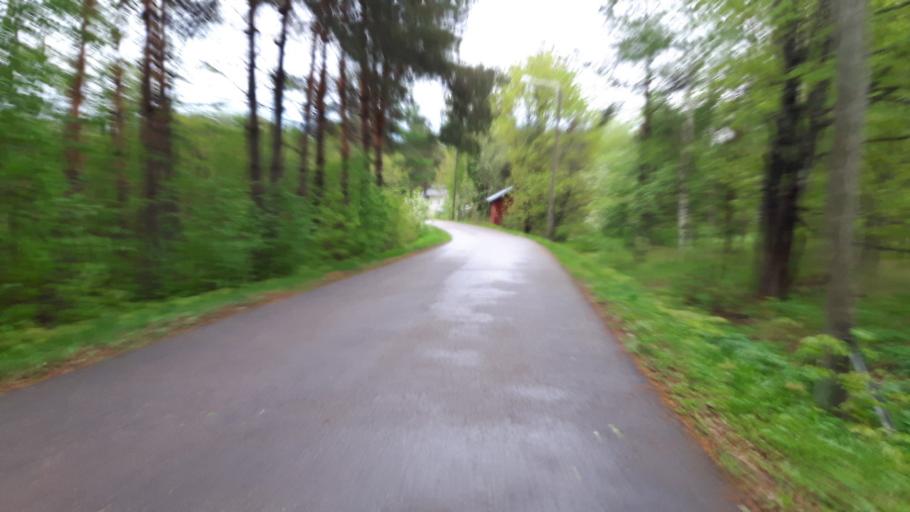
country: FI
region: Kymenlaakso
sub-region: Kotka-Hamina
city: Karhula
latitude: 60.5596
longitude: 27.0297
